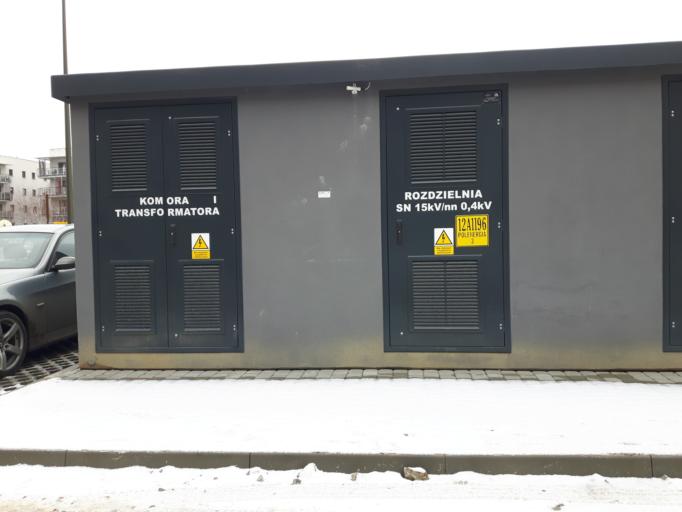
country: PL
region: Masovian Voivodeship
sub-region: Powiat wolominski
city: Zabki
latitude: 52.2752
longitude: 21.1179
